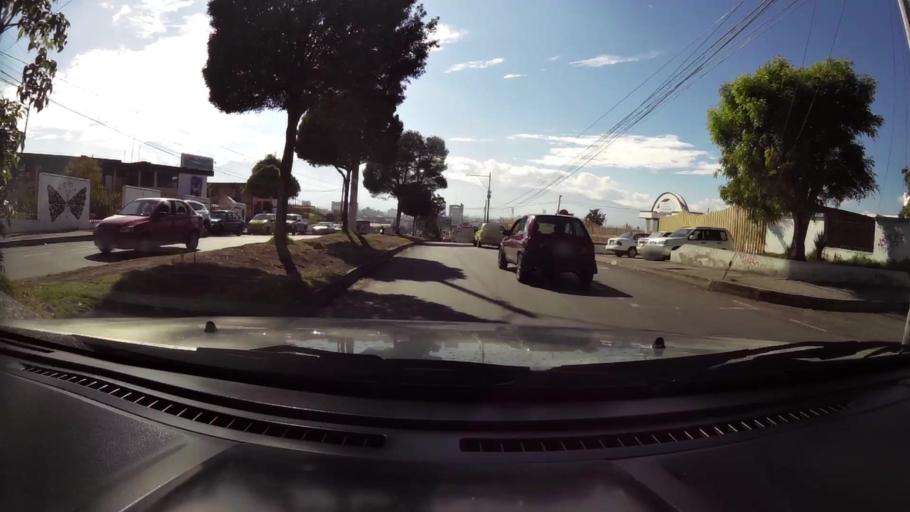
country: EC
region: Chimborazo
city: Riobamba
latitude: -1.6601
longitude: -78.6653
